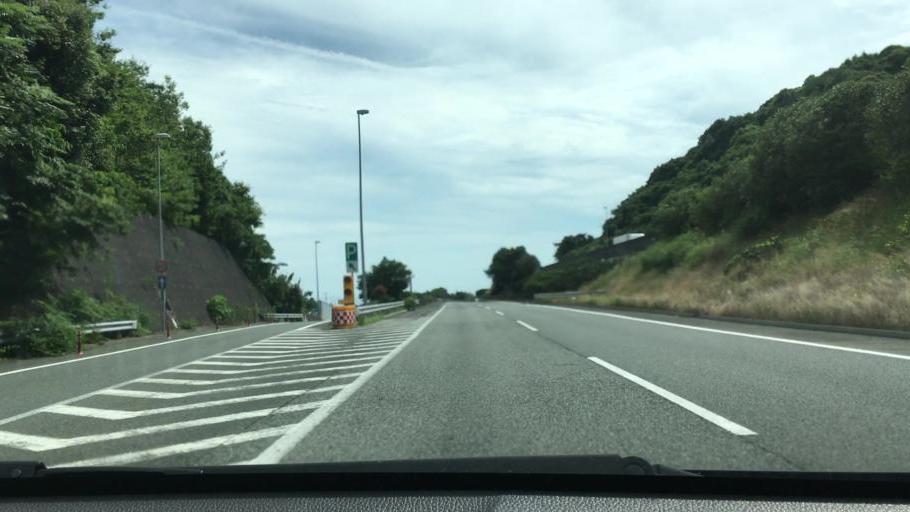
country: JP
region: Yamaguchi
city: Hofu
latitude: 34.0652
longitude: 131.6565
